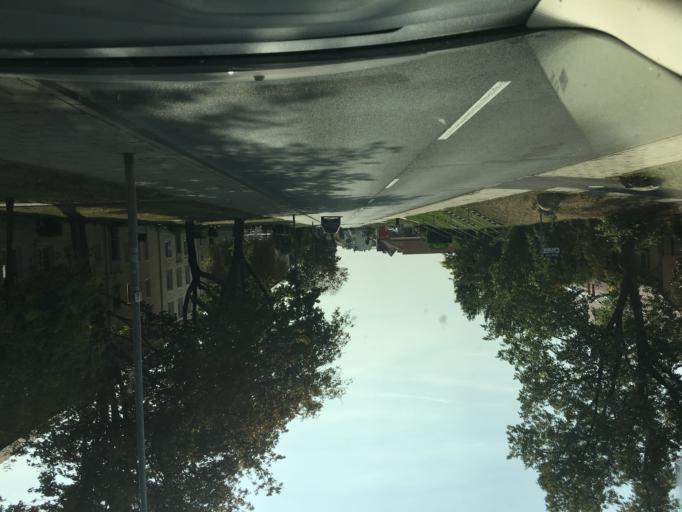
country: DE
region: Saxony-Anhalt
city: Calbe
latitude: 51.9152
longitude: 11.7875
